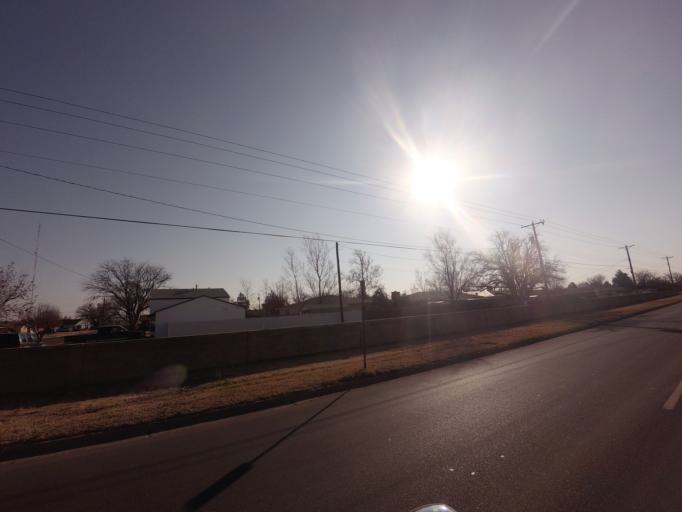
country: US
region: New Mexico
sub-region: Curry County
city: Clovis
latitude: 34.4151
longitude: -103.2142
